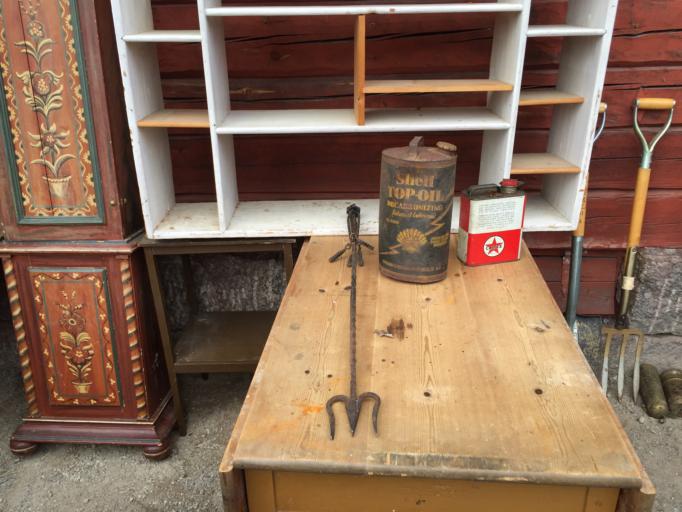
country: SE
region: Gaevleborg
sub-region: Ljusdals Kommun
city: Jaervsoe
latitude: 61.7088
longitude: 16.1881
